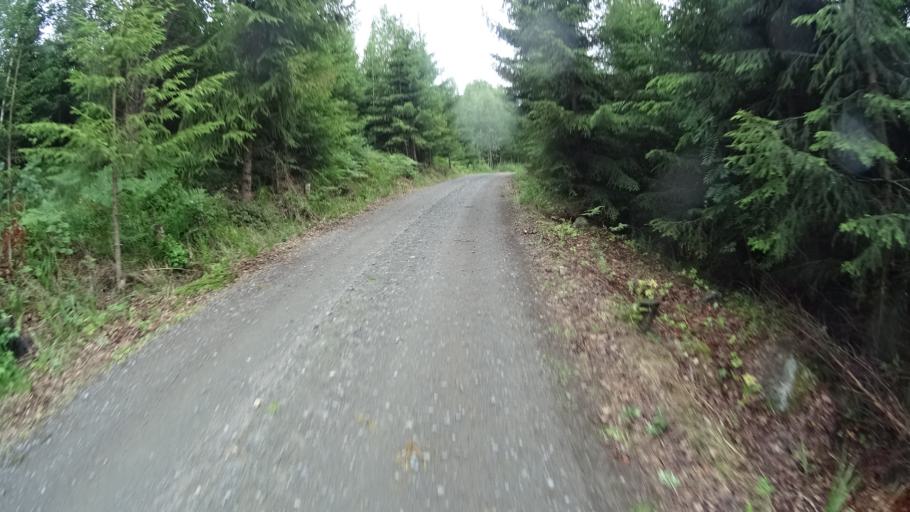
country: FI
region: Uusimaa
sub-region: Helsinki
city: Karkkila
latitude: 60.5809
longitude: 24.2836
